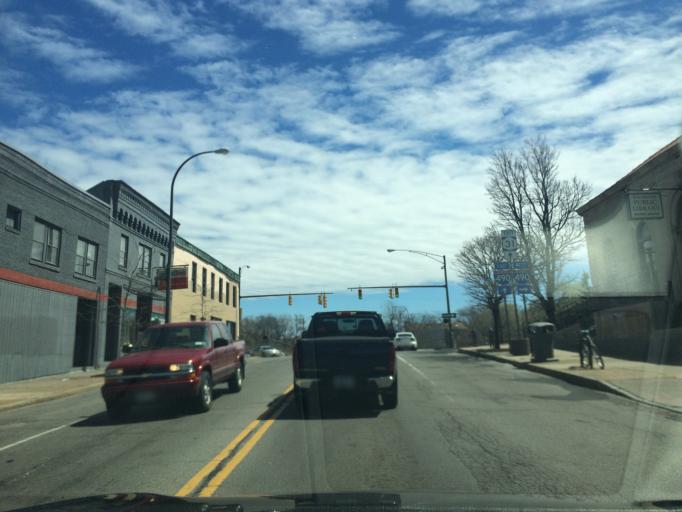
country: US
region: New York
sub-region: Monroe County
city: Rochester
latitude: 43.1428
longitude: -77.5871
